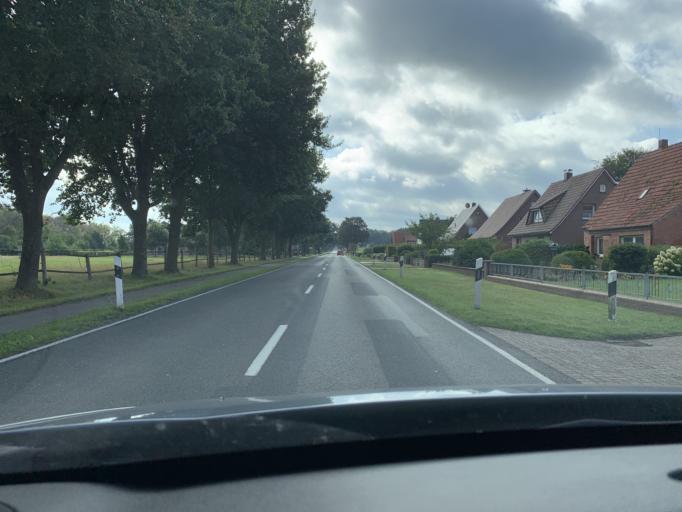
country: DE
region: Lower Saxony
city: Wardenburg
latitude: 53.0841
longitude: 8.1203
